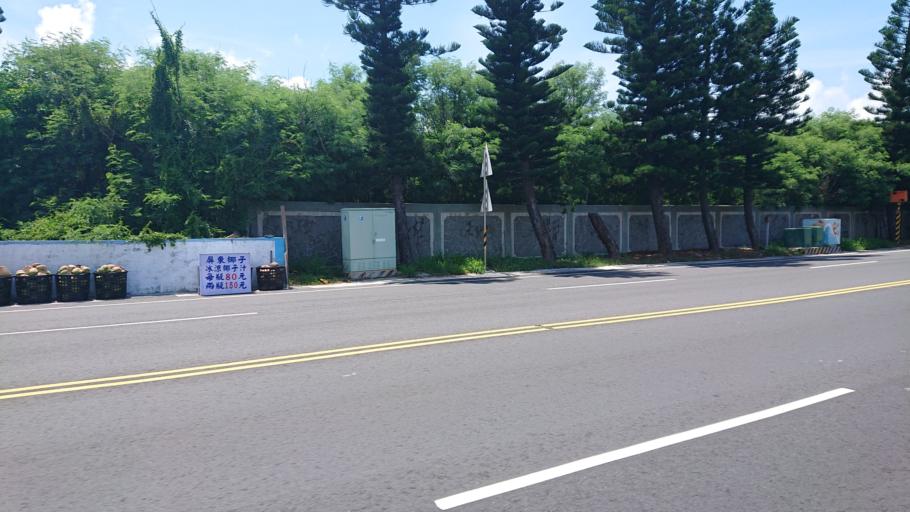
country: TW
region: Taiwan
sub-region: Penghu
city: Ma-kung
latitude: 23.6342
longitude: 119.5973
